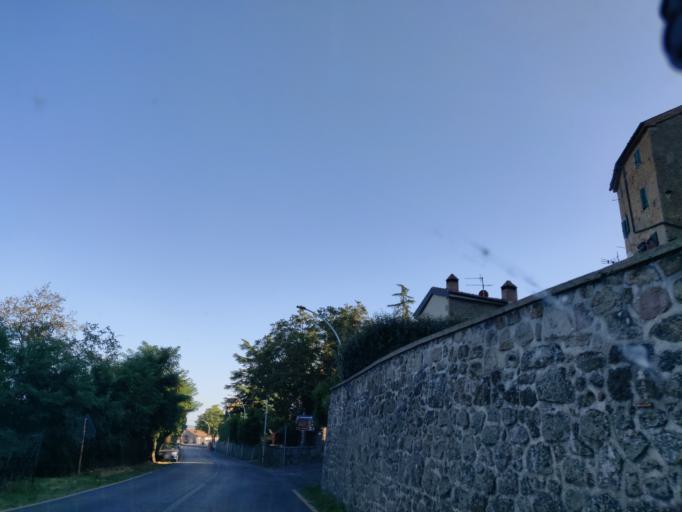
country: IT
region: Tuscany
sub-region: Provincia di Siena
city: Piancastagnaio
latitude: 42.8490
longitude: 11.6951
